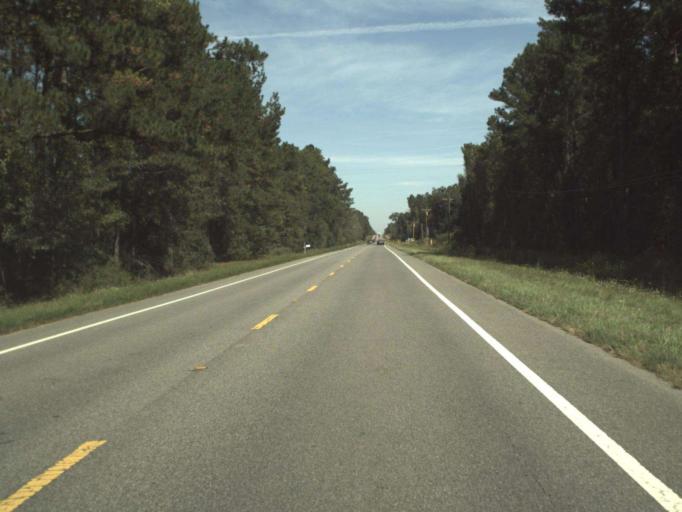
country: US
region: Florida
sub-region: Washington County
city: Chipley
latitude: 30.6495
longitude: -85.5824
